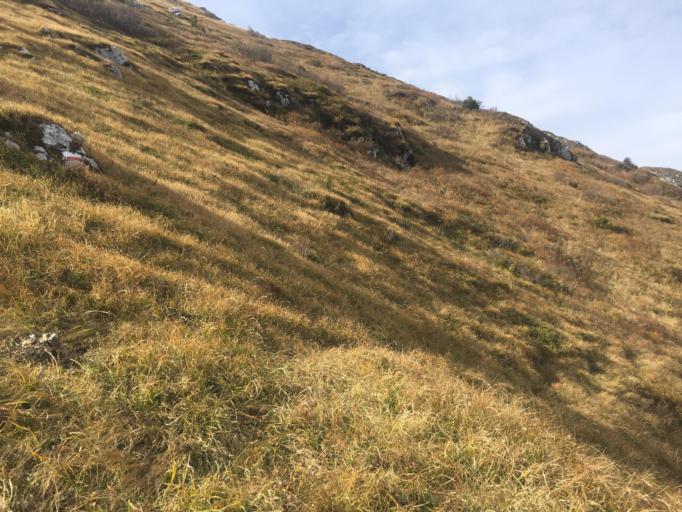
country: IT
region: Friuli Venezia Giulia
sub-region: Provincia di Udine
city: Preone
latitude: 46.3420
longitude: 12.8499
